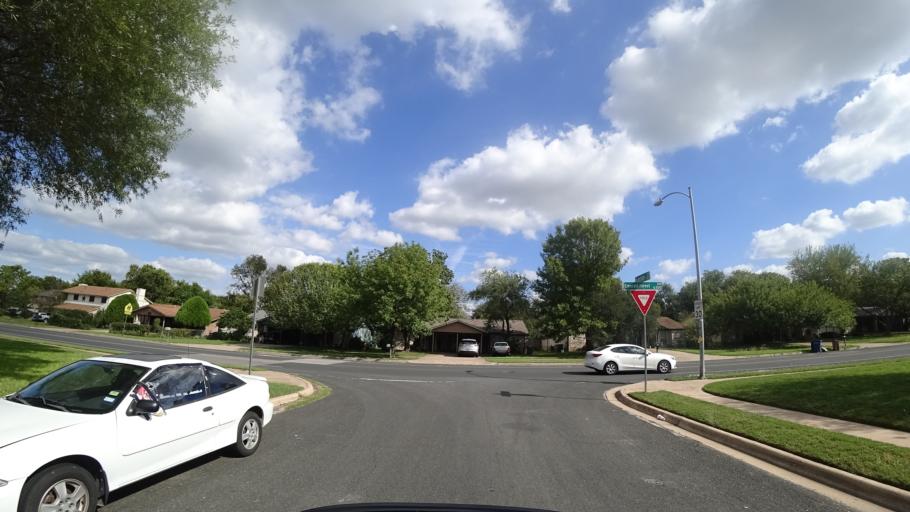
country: US
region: Texas
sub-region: Travis County
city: Onion Creek
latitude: 30.2049
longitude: -97.7916
